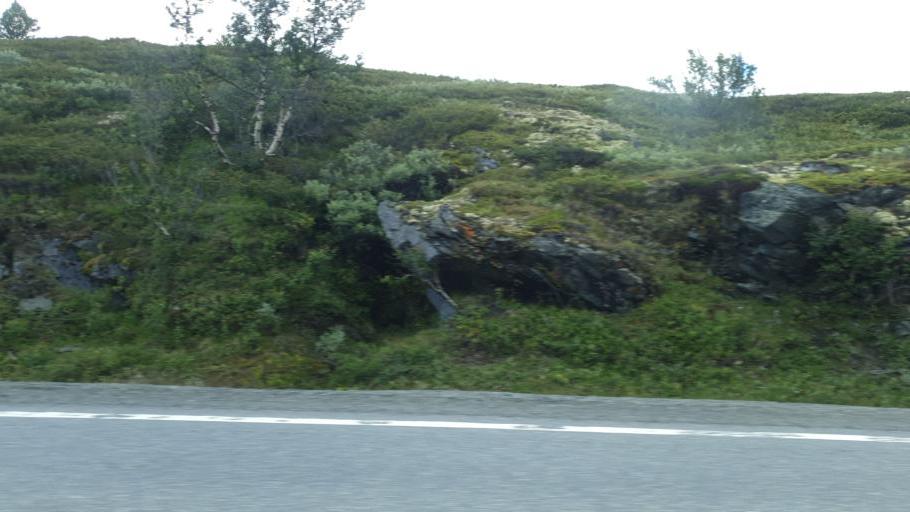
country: NO
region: Sor-Trondelag
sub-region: Oppdal
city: Oppdal
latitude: 62.2848
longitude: 9.6000
